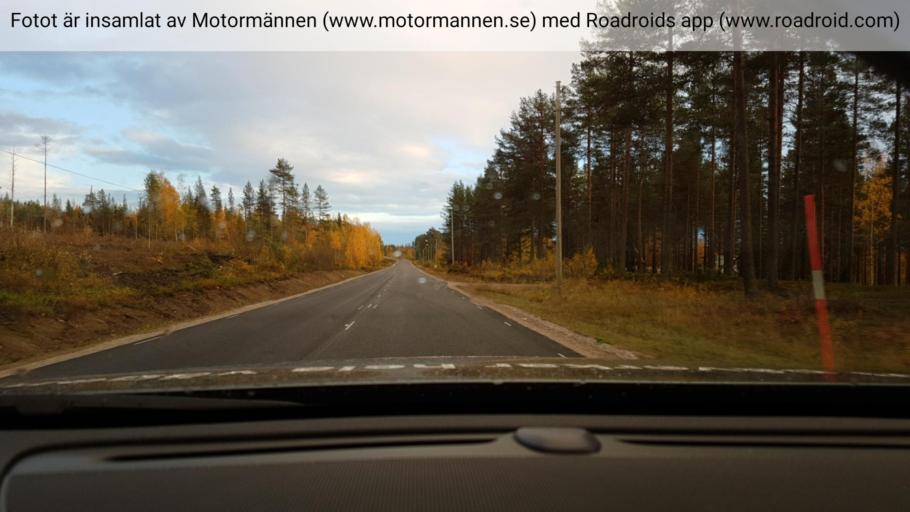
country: SE
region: Norrbotten
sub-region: Overkalix Kommun
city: OEverkalix
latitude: 66.3895
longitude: 22.8215
